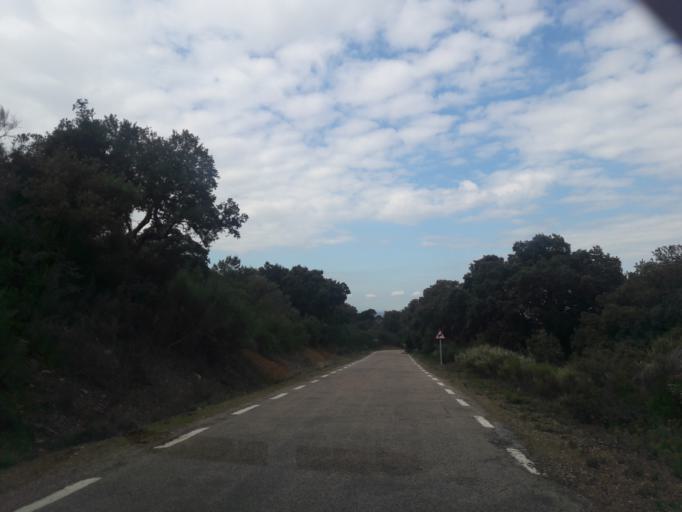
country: ES
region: Castille and Leon
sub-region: Provincia de Salamanca
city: Serradilla del Arroyo
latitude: 40.5405
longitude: -6.3950
